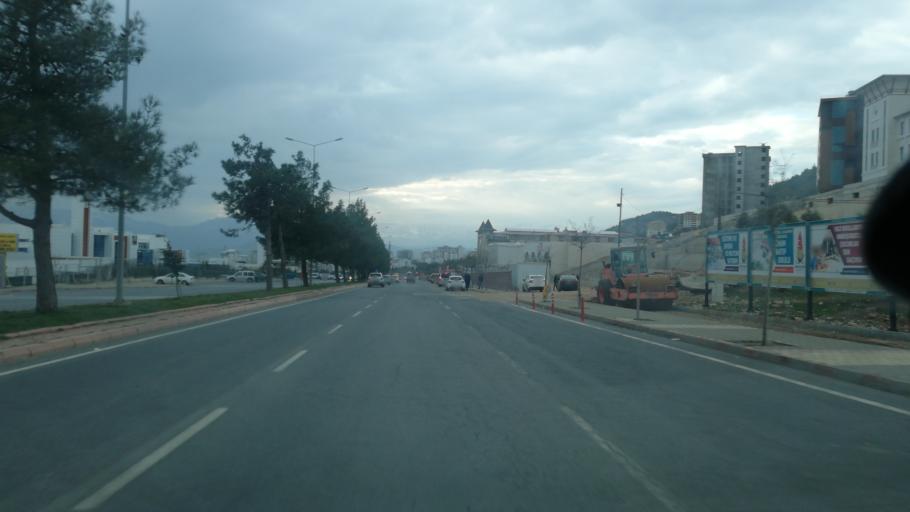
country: TR
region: Kahramanmaras
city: Kahramanmaras
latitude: 37.5988
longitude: 36.8411
